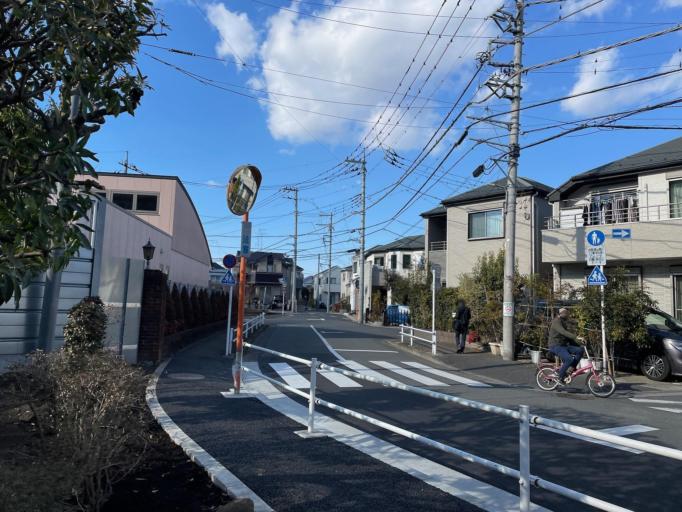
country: JP
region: Tokyo
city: Chofugaoka
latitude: 35.6412
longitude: 139.5526
